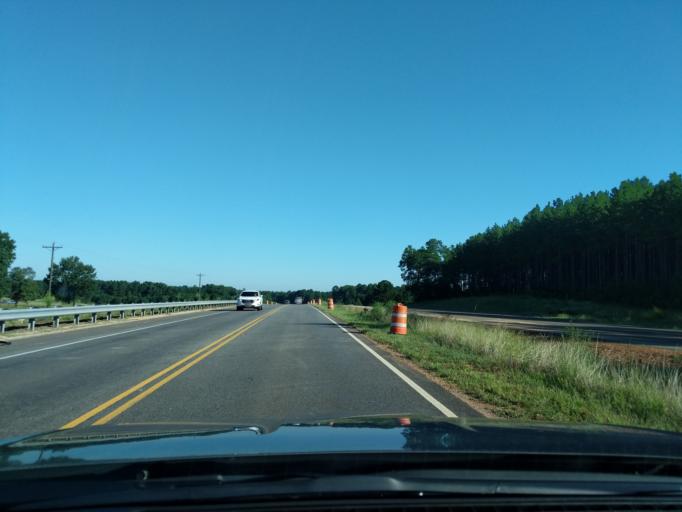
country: US
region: Georgia
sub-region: McDuffie County
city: Thomson
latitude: 33.5669
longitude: -82.5176
